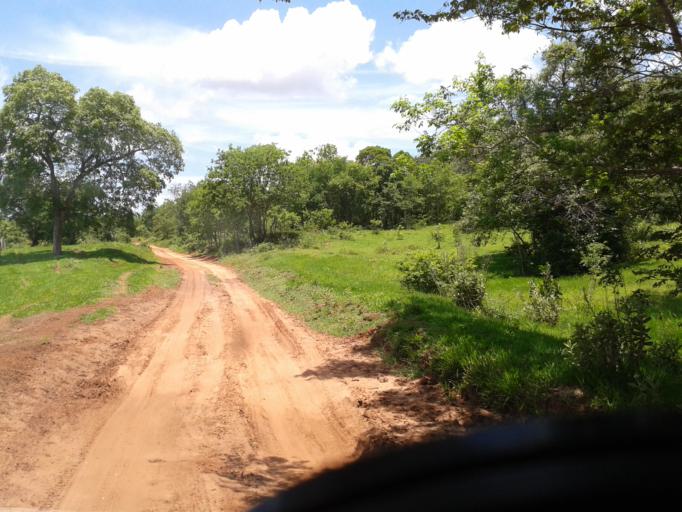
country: BR
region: Minas Gerais
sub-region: Santa Vitoria
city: Santa Vitoria
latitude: -18.9870
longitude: -49.8996
